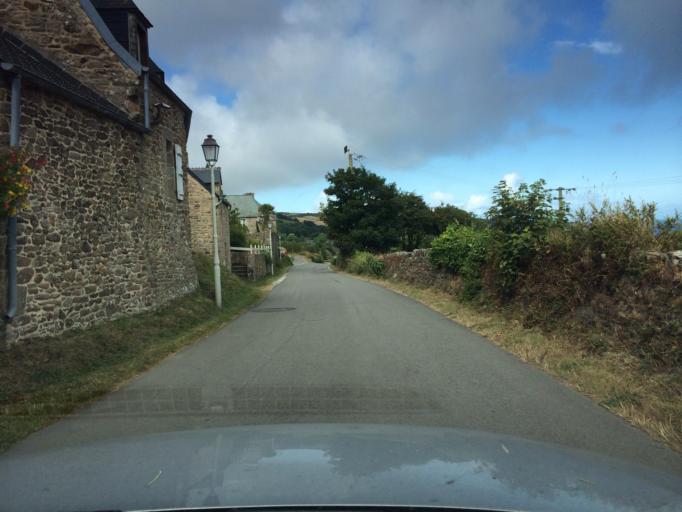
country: FR
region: Lower Normandy
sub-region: Departement de la Manche
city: Beaumont-Hague
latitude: 49.7010
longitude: -1.8746
